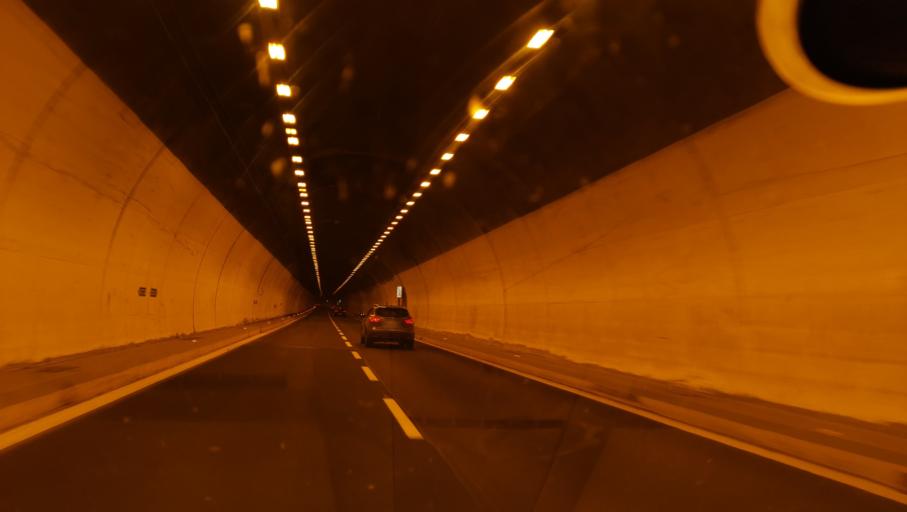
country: IT
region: Piedmont
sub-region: Provincia di Torino
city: Mattie
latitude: 45.1304
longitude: 7.1085
